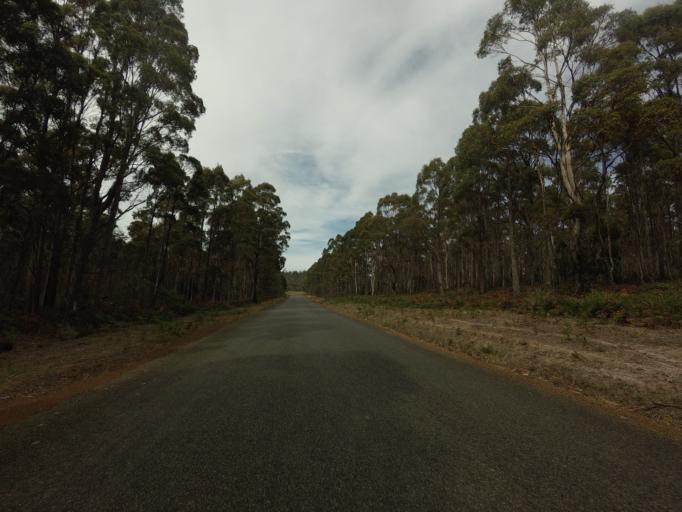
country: AU
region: Tasmania
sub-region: Sorell
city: Sorell
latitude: -42.5234
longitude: 147.6513
